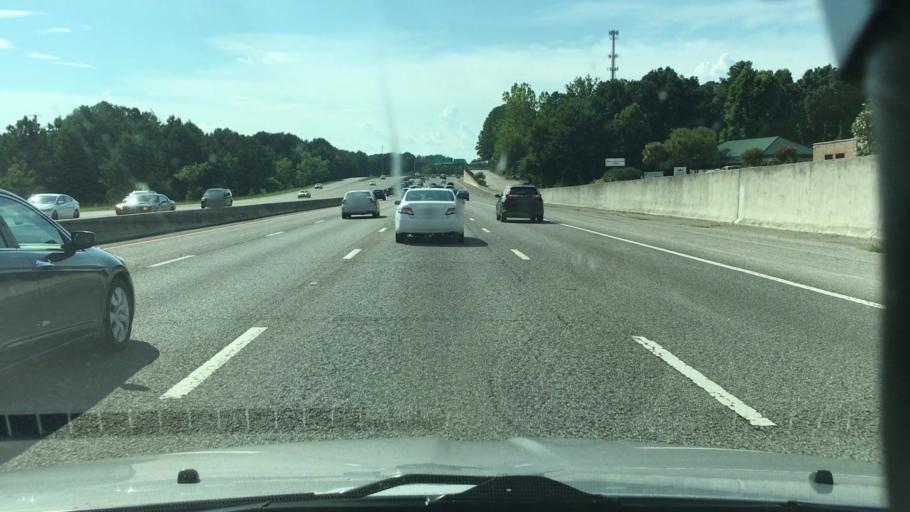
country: US
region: South Carolina
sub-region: Lexington County
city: West Columbia
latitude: 34.0165
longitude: -81.0870
